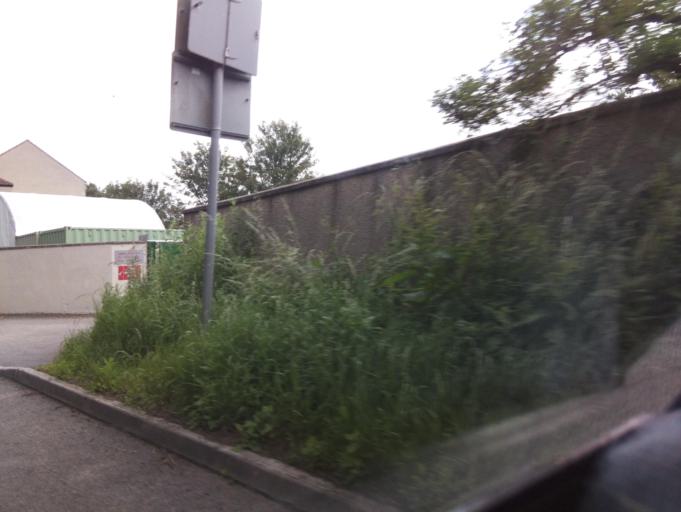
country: GB
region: England
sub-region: South Gloucestershire
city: Bitton
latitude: 51.4156
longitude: -2.4392
